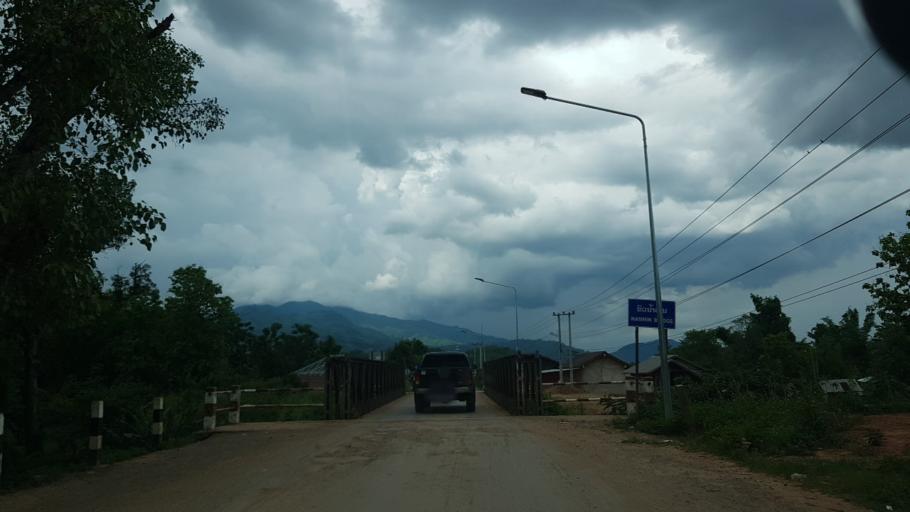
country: LA
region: Oudomxai
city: Muang Xay
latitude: 20.6740
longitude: 101.9683
